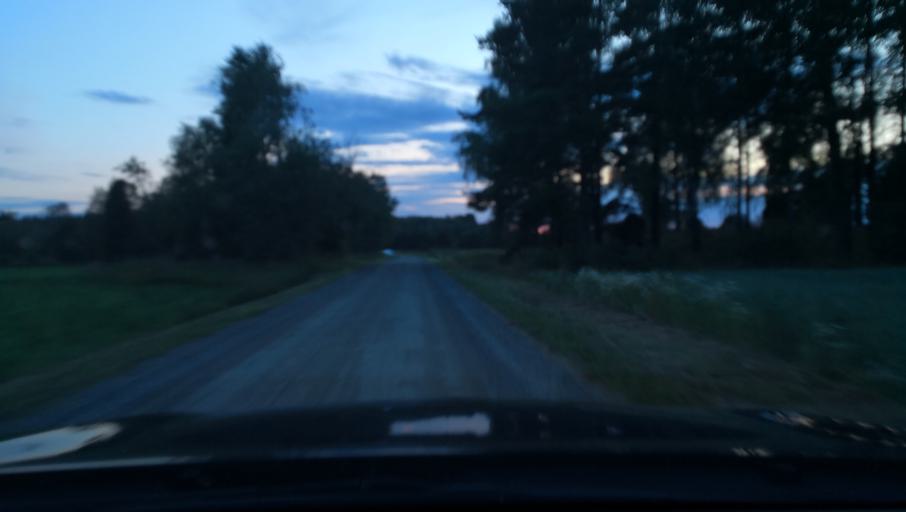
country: SE
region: Uppsala
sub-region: Osthammars Kommun
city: Bjorklinge
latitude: 60.0025
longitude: 17.3537
